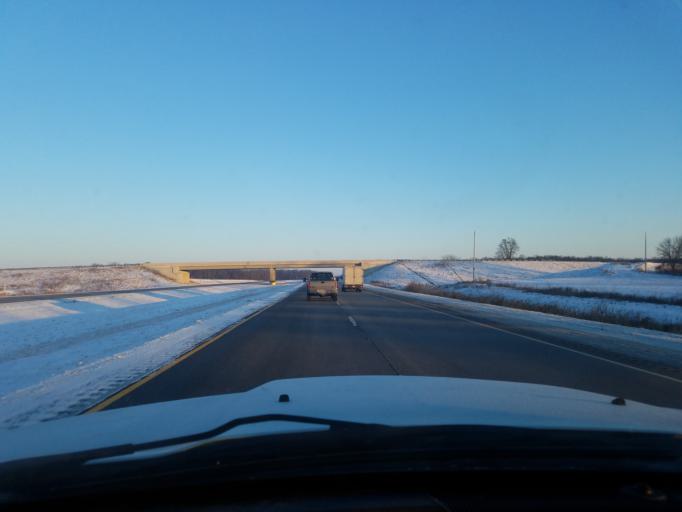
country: US
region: Indiana
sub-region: Marshall County
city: Plymouth
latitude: 41.4141
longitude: -86.2978
